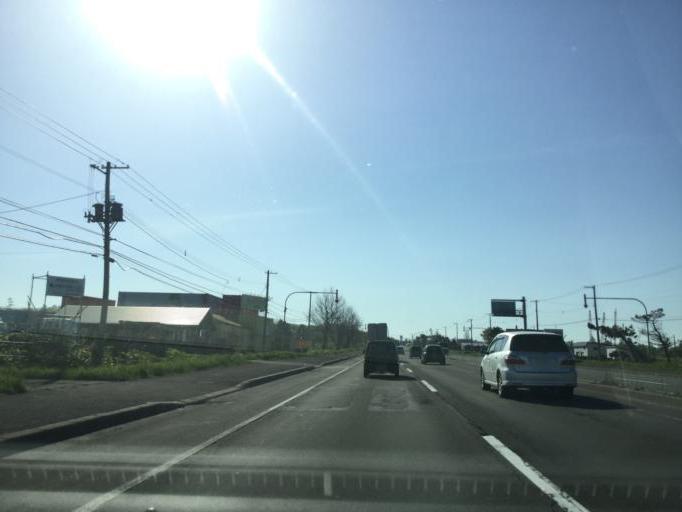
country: JP
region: Hokkaido
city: Kitahiroshima
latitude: 43.0108
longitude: 141.5124
